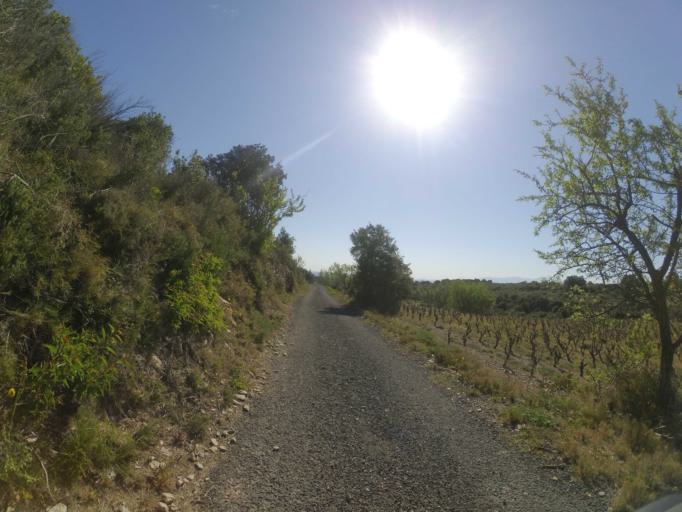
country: FR
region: Languedoc-Roussillon
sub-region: Departement des Pyrenees-Orientales
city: Baixas
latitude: 42.7620
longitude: 2.7649
